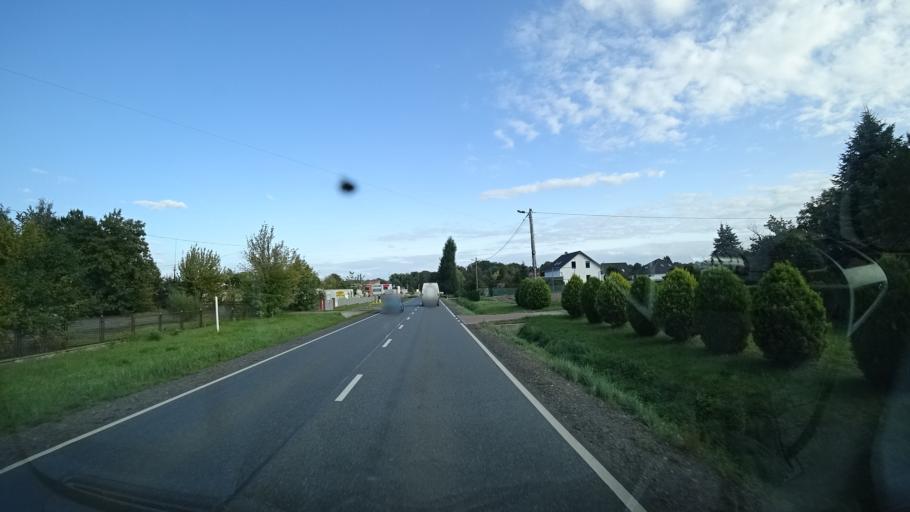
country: PL
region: Silesian Voivodeship
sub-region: Powiat gliwicki
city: Sosnicowice
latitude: 50.2760
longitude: 18.5210
